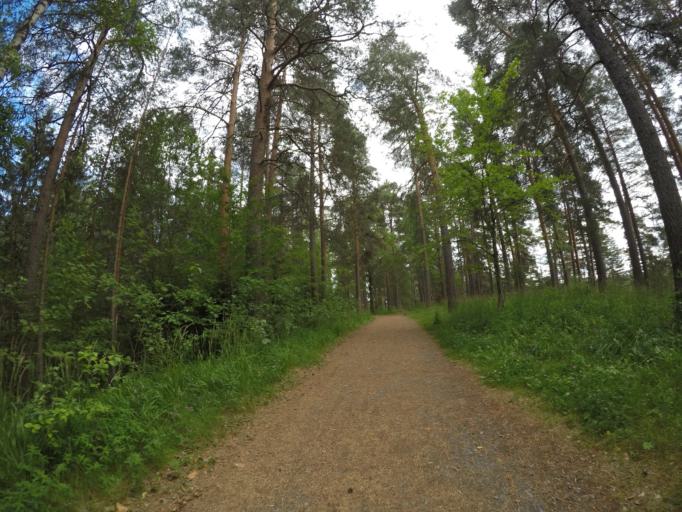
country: FI
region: Haeme
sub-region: Haemeenlinna
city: Haemeenlinna
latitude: 60.9967
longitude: 24.4203
